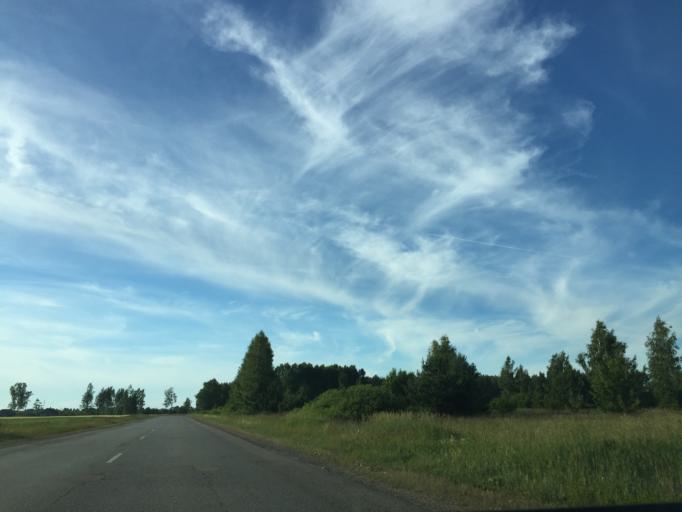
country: LV
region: Ventspils
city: Ventspils
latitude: 57.2903
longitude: 21.5653
